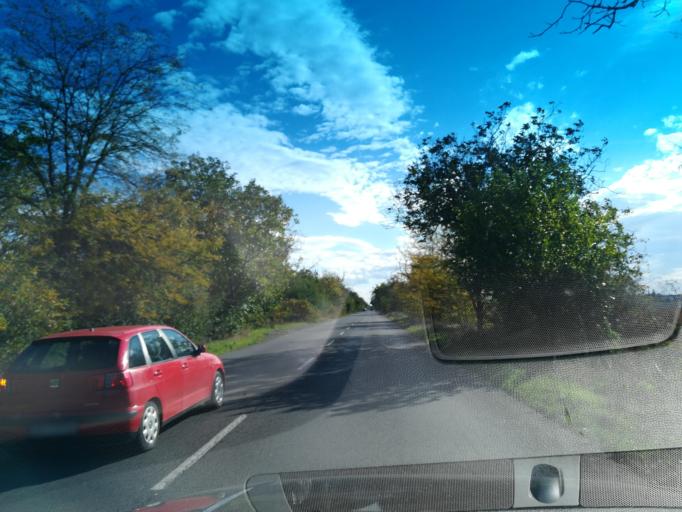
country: BG
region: Stara Zagora
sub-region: Obshtina Stara Zagora
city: Stara Zagora
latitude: 42.3726
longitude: 25.6526
